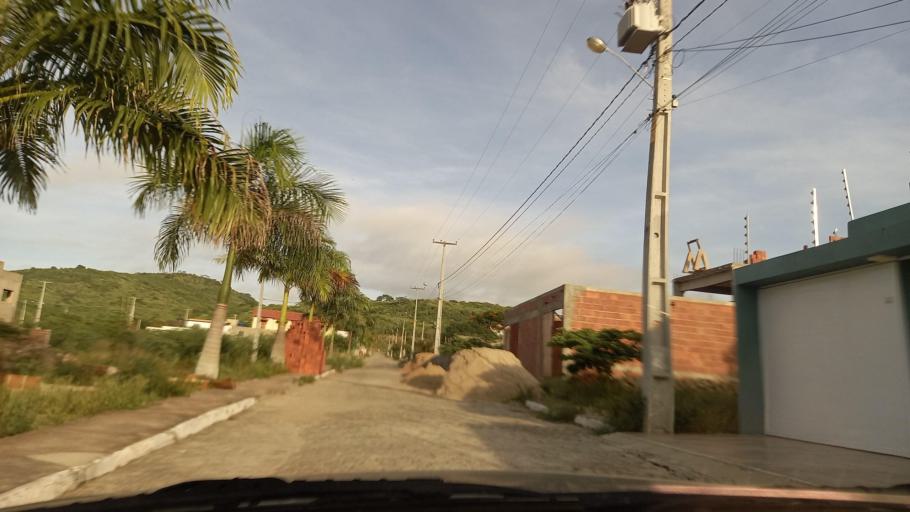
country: BR
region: Pernambuco
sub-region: Bezerros
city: Bezerros
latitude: -8.2169
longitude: -35.7503
